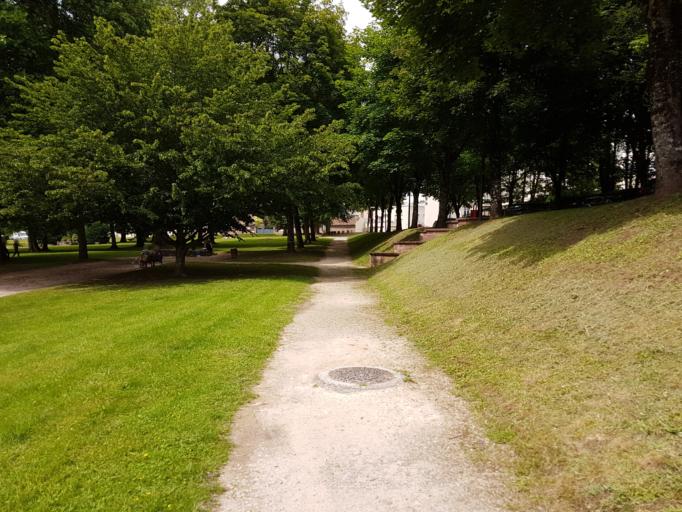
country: FR
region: Franche-Comte
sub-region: Departement de la Haute-Saone
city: Luxeuil-les-Bains
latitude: 47.8208
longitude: 6.3779
